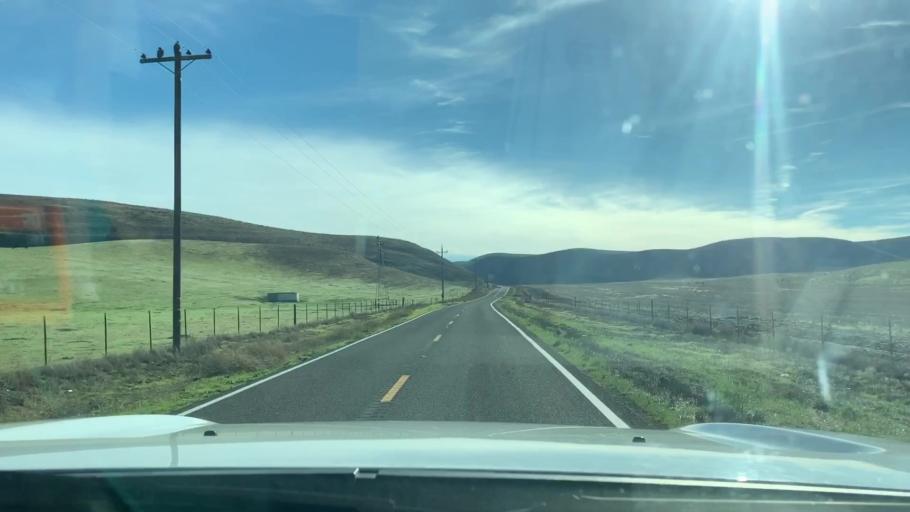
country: US
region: California
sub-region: Monterey County
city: King City
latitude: 36.1555
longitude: -120.9768
